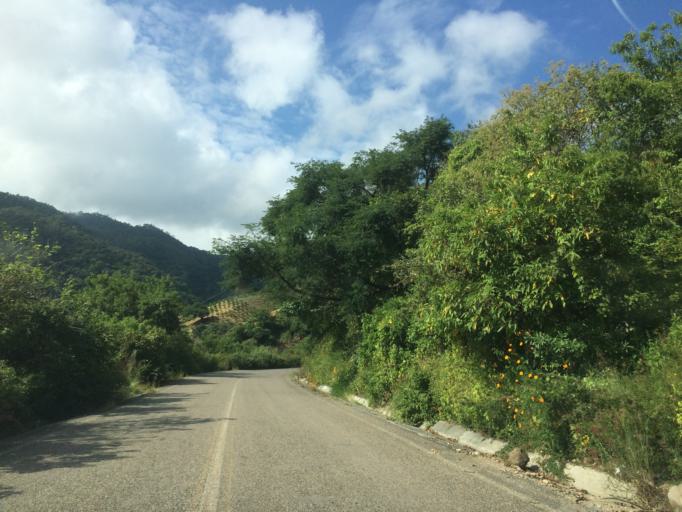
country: MX
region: Nayarit
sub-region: Ahuacatlan
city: Ahuacatlan
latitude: 21.0077
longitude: -104.4794
